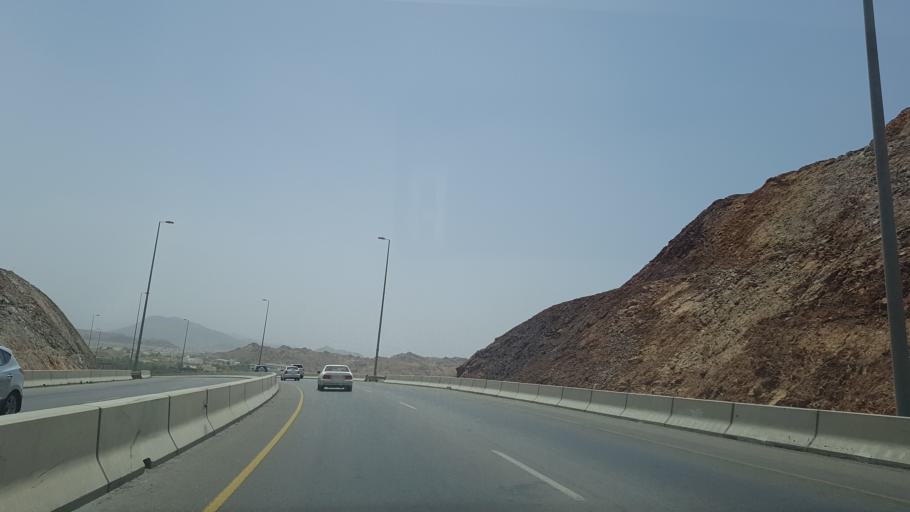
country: OM
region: Muhafazat ad Dakhiliyah
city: Bidbid
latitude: 23.4575
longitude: 58.1164
